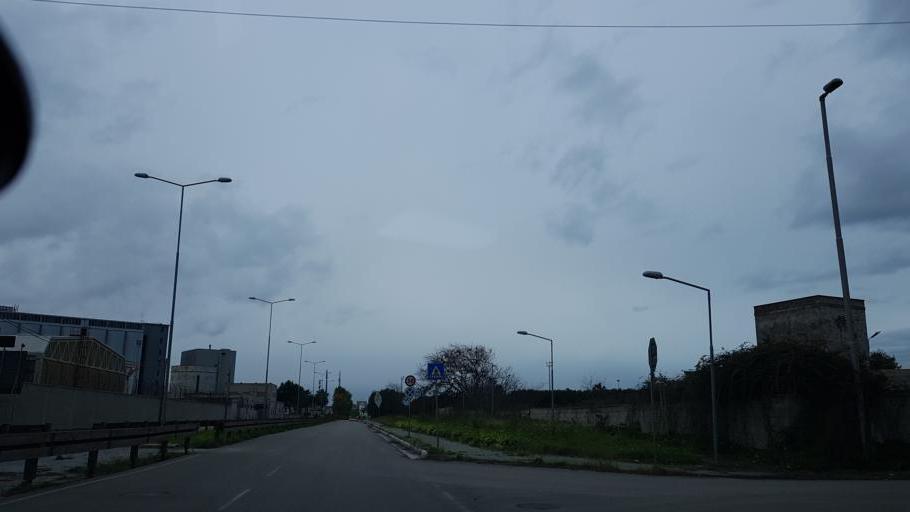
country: IT
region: Apulia
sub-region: Provincia di Brindisi
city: Materdomini
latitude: 40.6387
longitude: 17.9579
